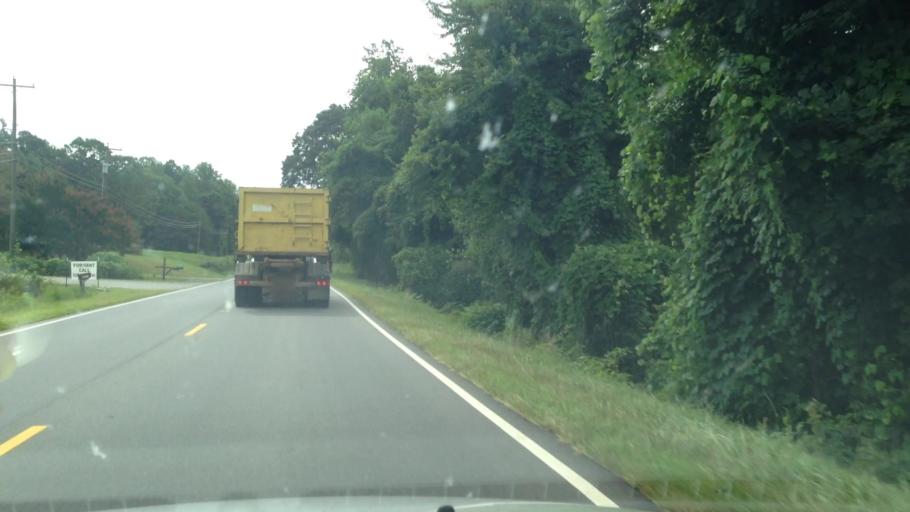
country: US
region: North Carolina
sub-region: Rockingham County
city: Reidsville
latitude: 36.3673
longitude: -79.7171
